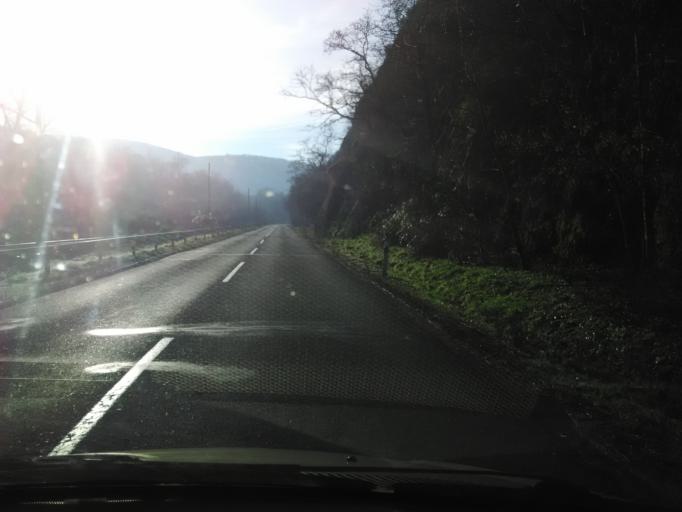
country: SK
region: Nitriansky
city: Tlmace
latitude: 48.3398
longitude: 18.5578
